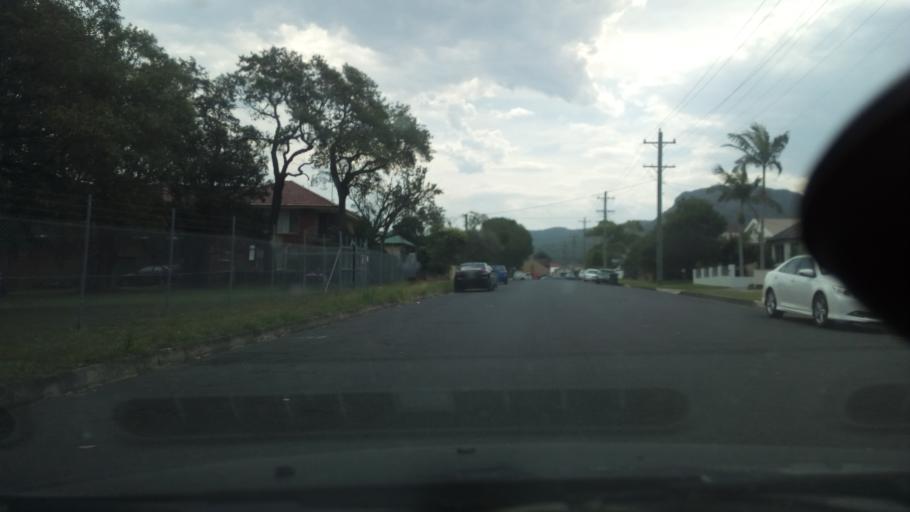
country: AU
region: New South Wales
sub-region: Wollongong
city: Gwynneville
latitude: -34.4163
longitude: 150.8873
